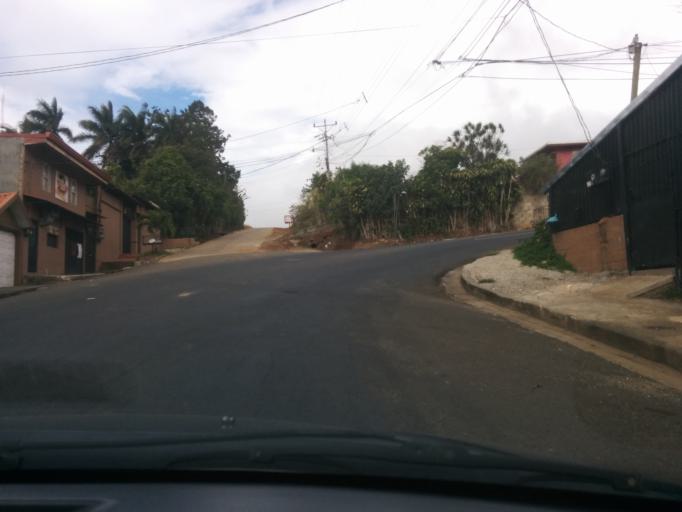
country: CR
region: Alajuela
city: San Ramon
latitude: 10.0829
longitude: -84.4755
